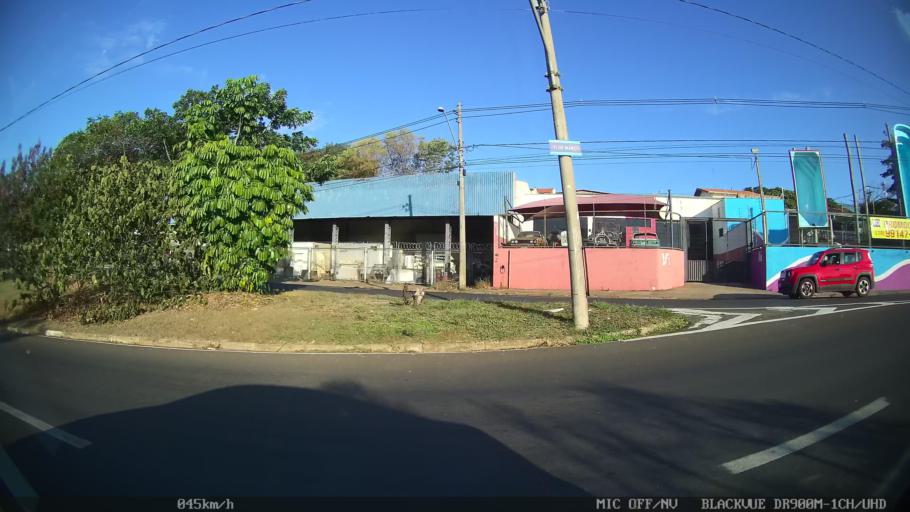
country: BR
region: Sao Paulo
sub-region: Piracicaba
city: Piracicaba
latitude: -22.7575
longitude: -47.6437
